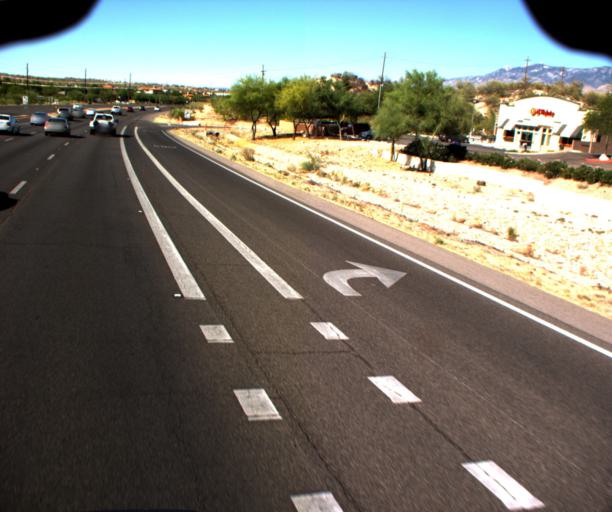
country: US
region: Arizona
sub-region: Pima County
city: Oro Valley
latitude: 32.3905
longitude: -110.9637
